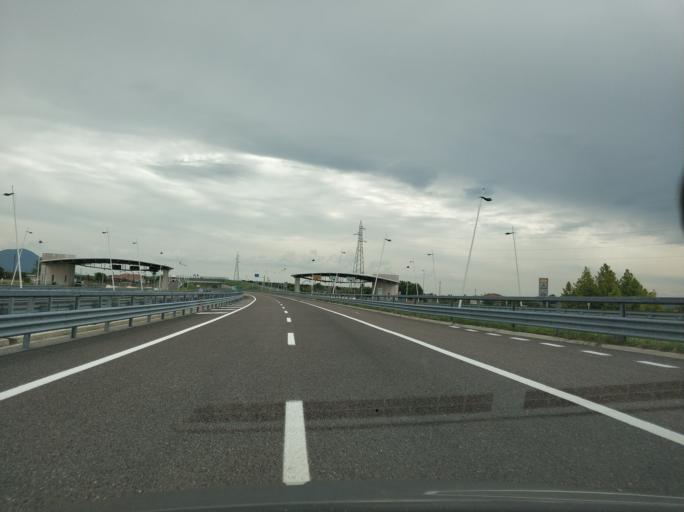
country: IT
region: Veneto
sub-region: Provincia di Vicenza
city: Villaganzerla
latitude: 45.4580
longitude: 11.6294
